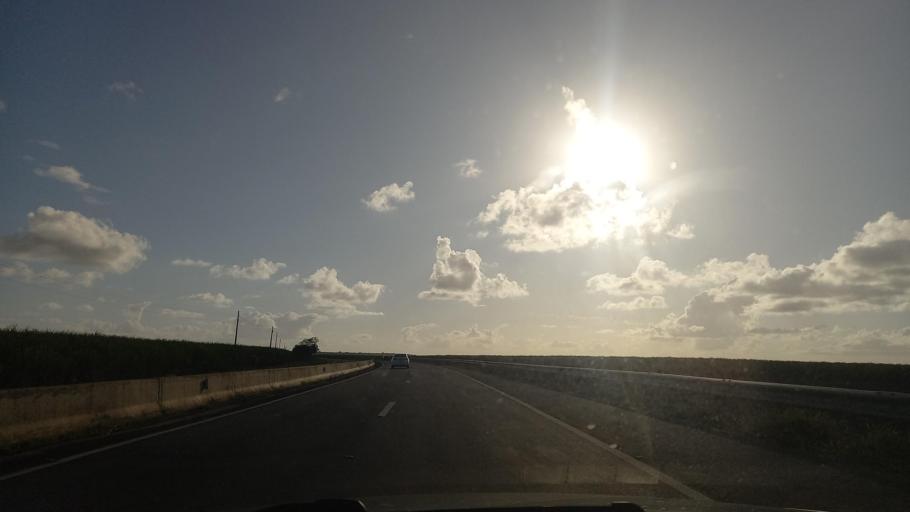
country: BR
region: Alagoas
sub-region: Sao Miguel Dos Campos
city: Sao Miguel dos Campos
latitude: -9.7998
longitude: -36.1646
